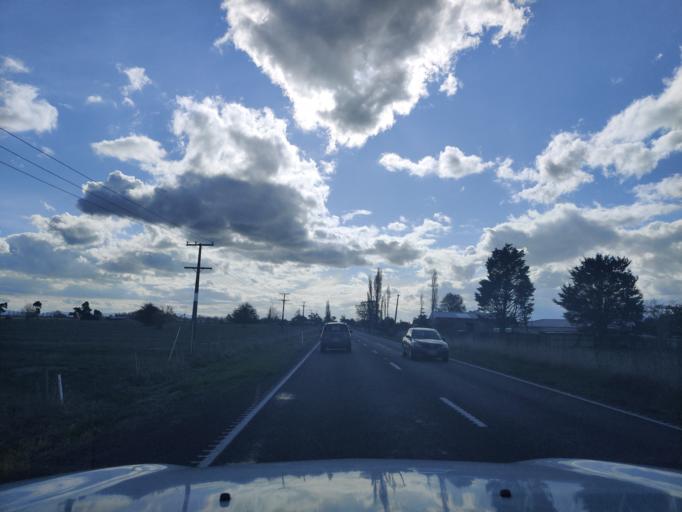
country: NZ
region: Waikato
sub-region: Hauraki District
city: Ngatea
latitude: -37.2895
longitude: 175.5489
